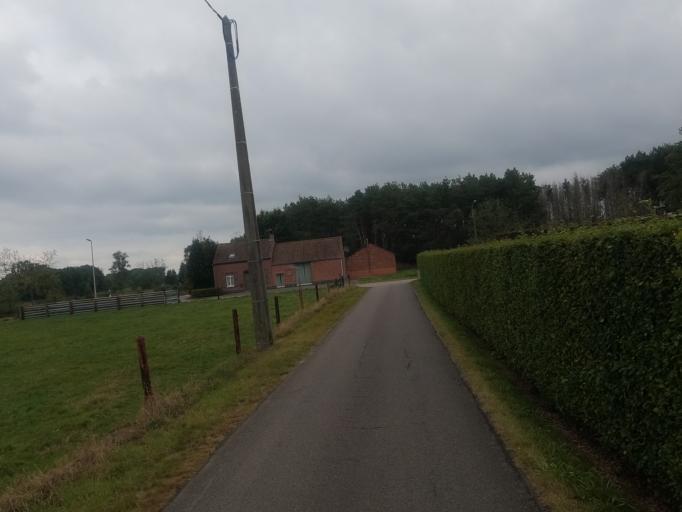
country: BE
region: Flanders
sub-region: Provincie Antwerpen
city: Nijlen
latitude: 51.1441
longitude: 4.6615
